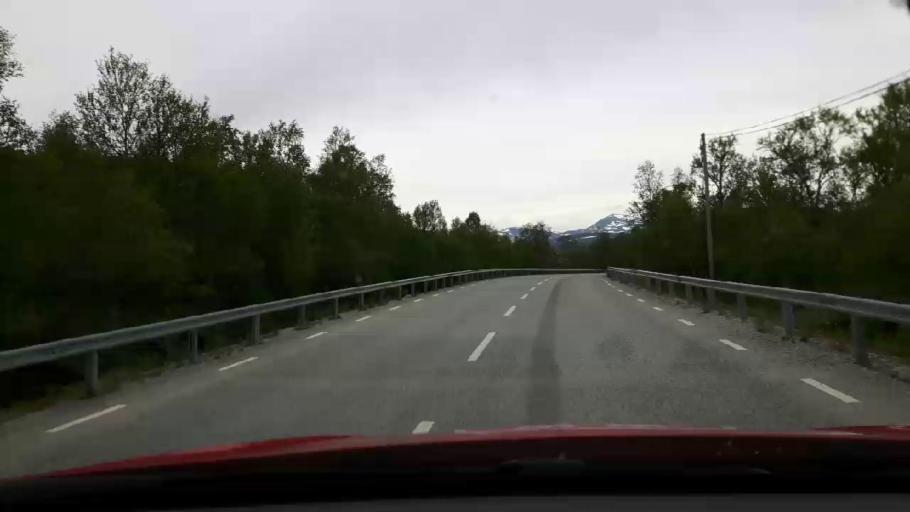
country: NO
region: Sor-Trondelag
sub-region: Tydal
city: Aas
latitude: 62.6981
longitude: 12.3963
